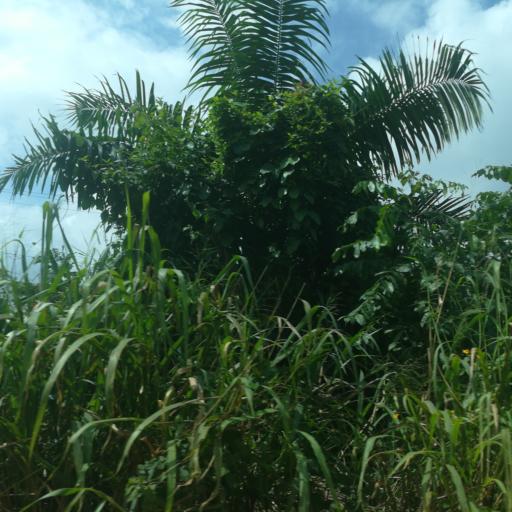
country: NG
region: Ogun
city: Odogbolu
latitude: 6.6522
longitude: 3.7019
